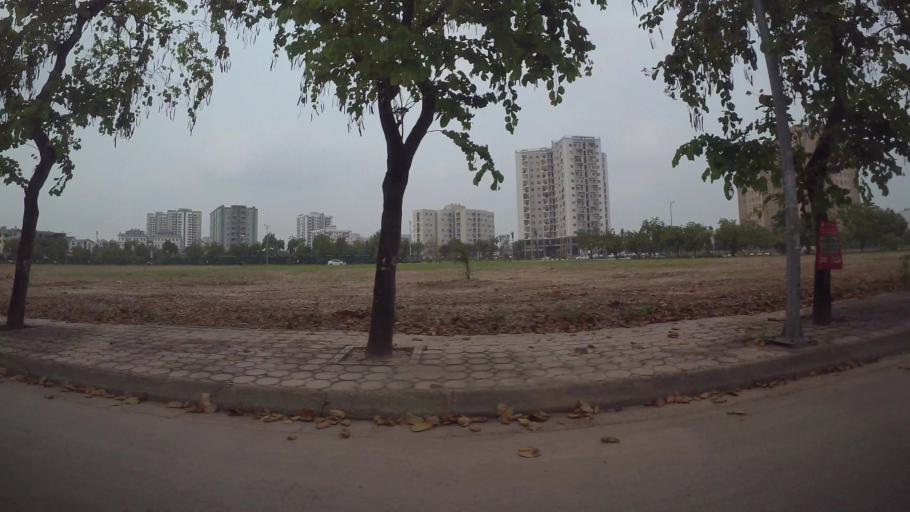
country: VN
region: Ha Noi
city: Trau Quy
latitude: 21.0582
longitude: 105.9127
